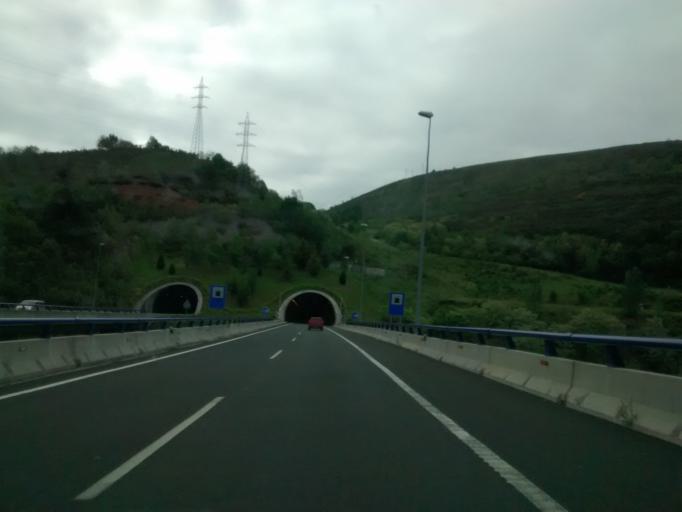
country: ES
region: Cantabria
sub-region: Provincia de Cantabria
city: Los Corrales de Buelna
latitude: 43.2251
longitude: -4.0791
